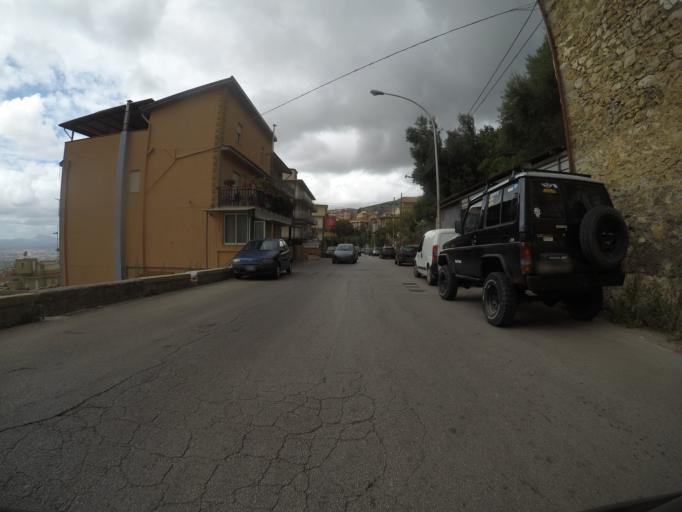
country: IT
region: Sicily
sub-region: Palermo
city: Montelepre
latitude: 38.0922
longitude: 13.1757
